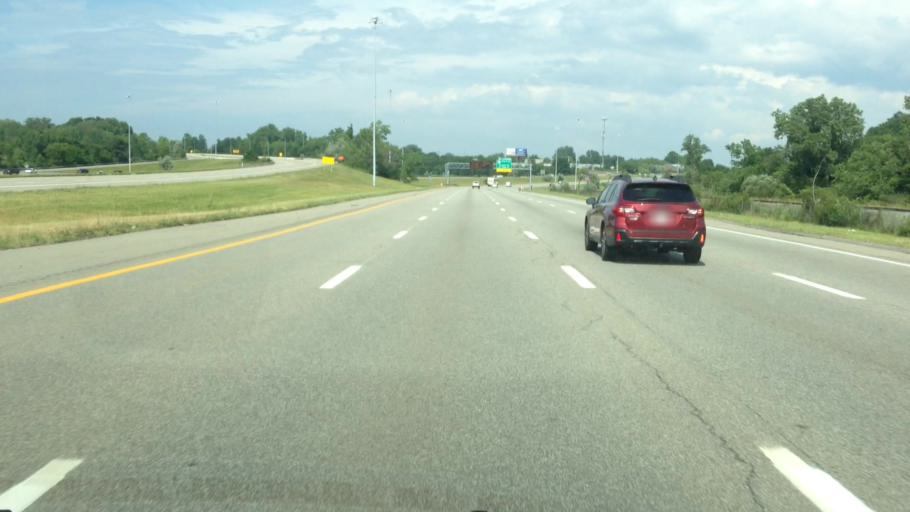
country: US
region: Ohio
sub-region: Cuyahoga County
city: Brooklyn
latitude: 41.4489
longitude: -81.7345
